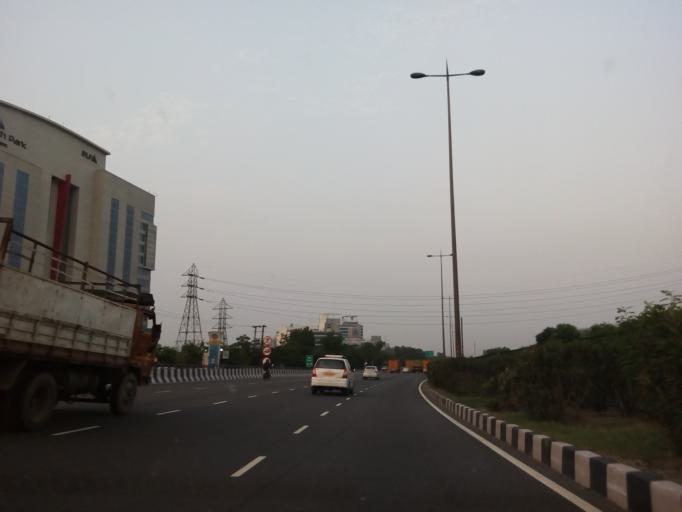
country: IN
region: Haryana
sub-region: Gurgaon
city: Gurgaon
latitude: 28.4663
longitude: 77.0557
